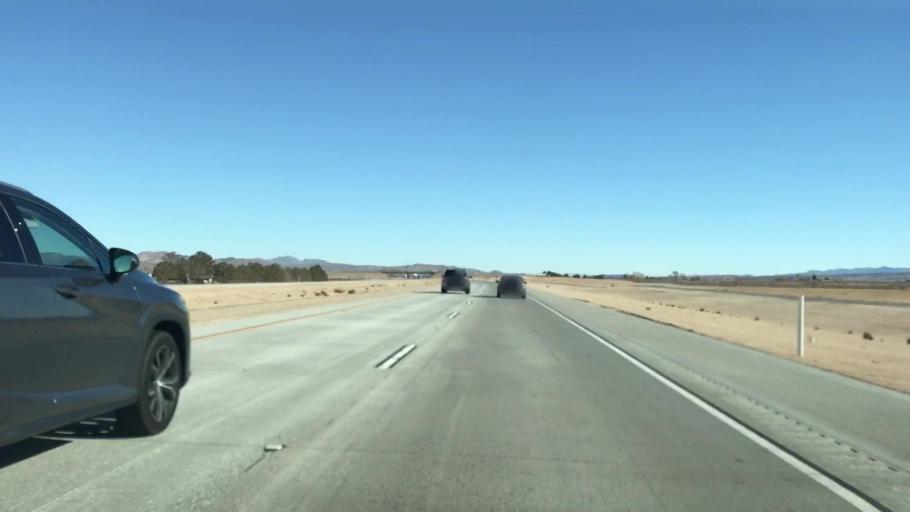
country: US
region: California
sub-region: San Bernardino County
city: Lenwood
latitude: 34.9135
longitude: -117.2031
